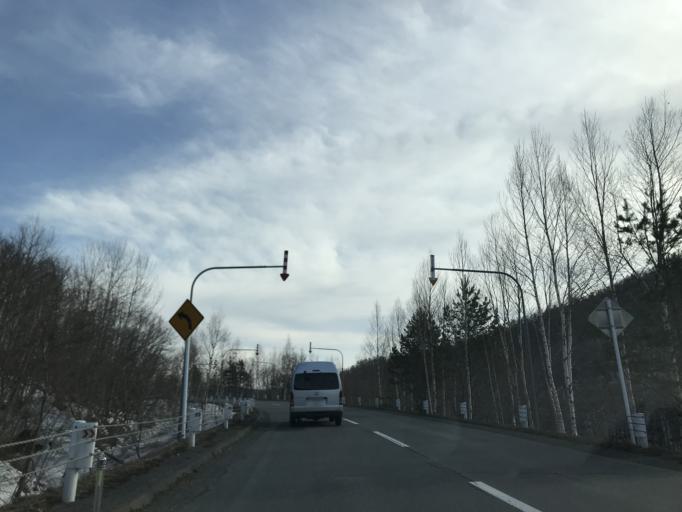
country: JP
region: Hokkaido
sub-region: Asahikawa-shi
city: Asahikawa
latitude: 43.7204
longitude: 142.3187
